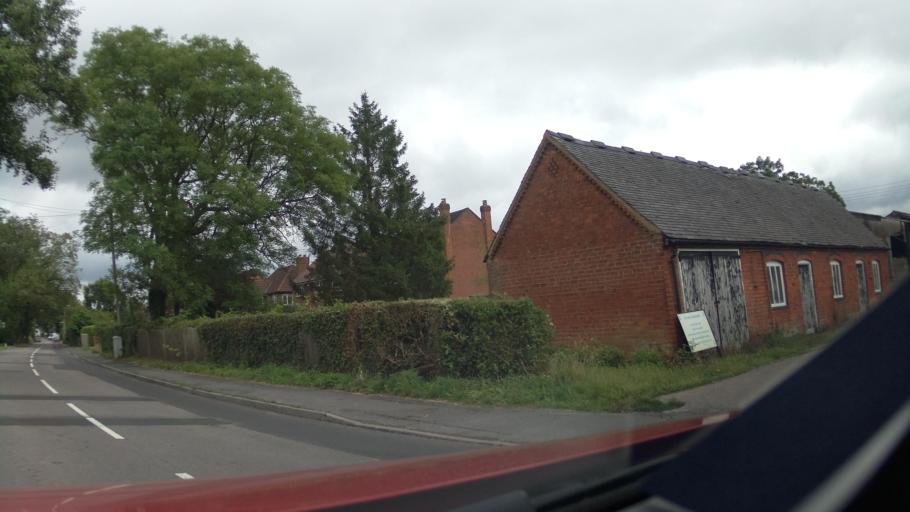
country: GB
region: England
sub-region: Solihull
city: Tidbury Green
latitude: 52.3767
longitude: -1.8731
